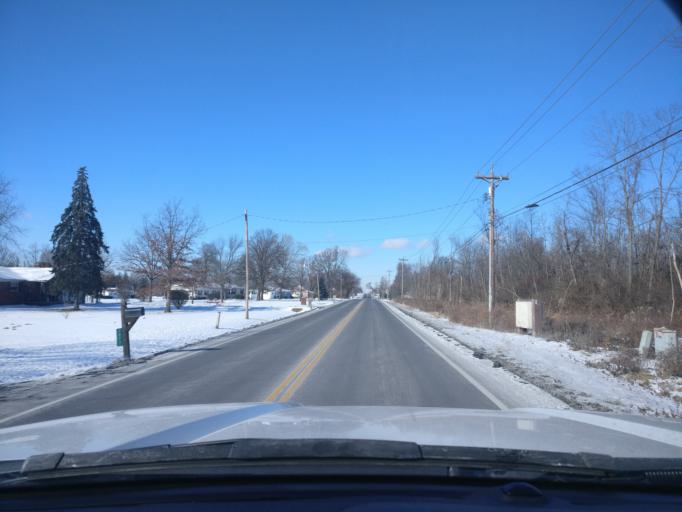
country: US
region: Ohio
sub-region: Warren County
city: Hunter
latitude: 39.4963
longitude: -84.2561
